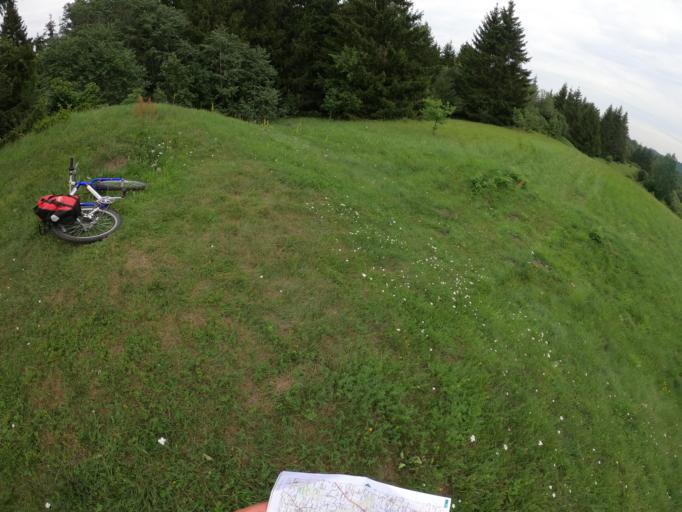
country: LT
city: Ariogala
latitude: 55.3098
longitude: 23.3824
